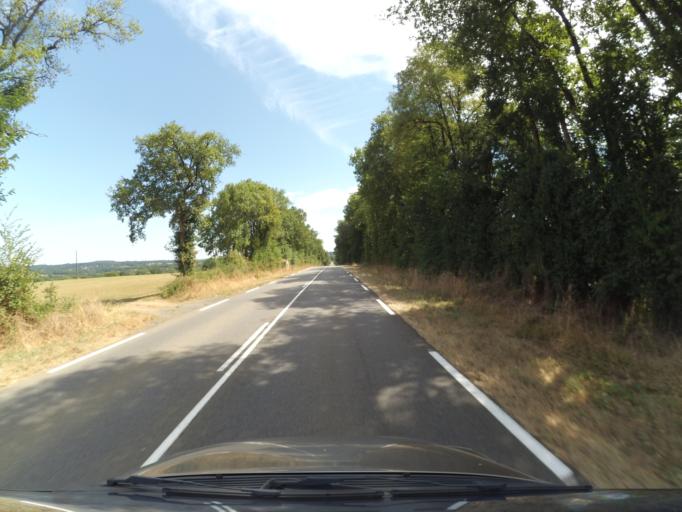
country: FR
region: Poitou-Charentes
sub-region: Departement de la Charente
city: Confolens
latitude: 45.9786
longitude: 0.6842
